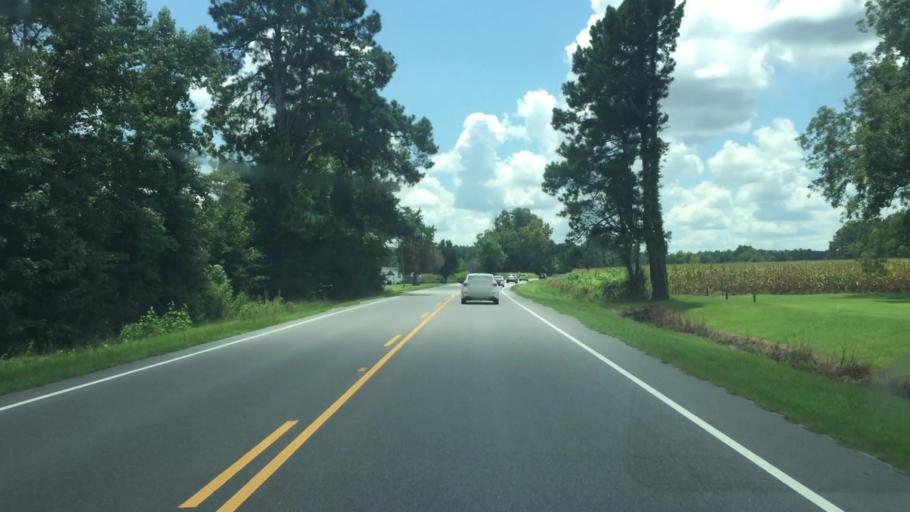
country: US
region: North Carolina
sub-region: Columbus County
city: Tabor City
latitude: 34.1891
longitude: -78.8367
